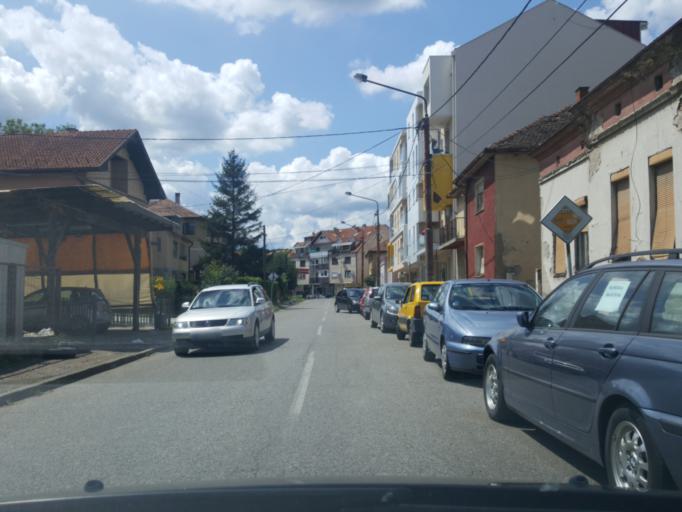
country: RS
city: Trsic
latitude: 44.5284
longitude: 19.2237
